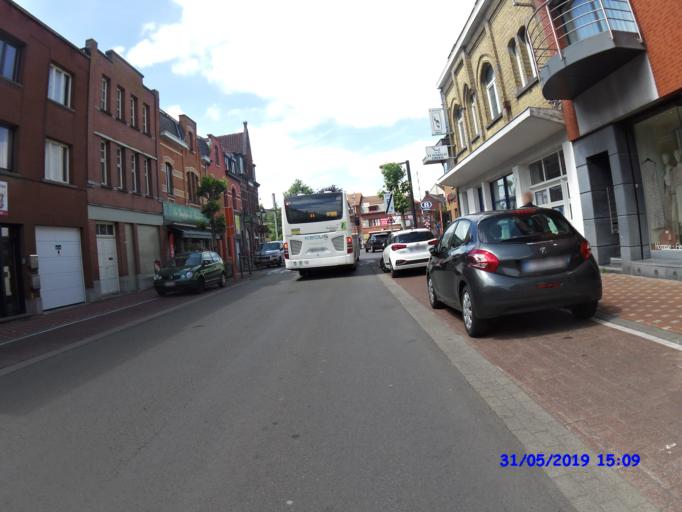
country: FR
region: Nord-Pas-de-Calais
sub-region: Departement du Nord
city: Comines
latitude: 50.7709
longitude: 2.9978
